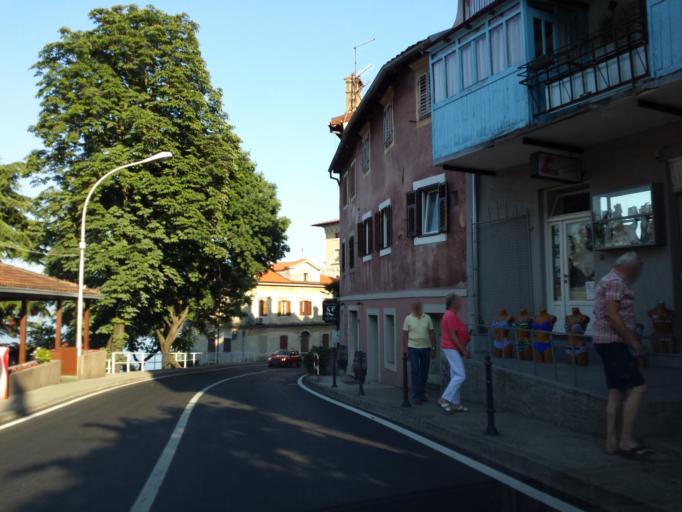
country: HR
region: Istarska
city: Lovran
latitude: 45.2922
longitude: 14.2767
